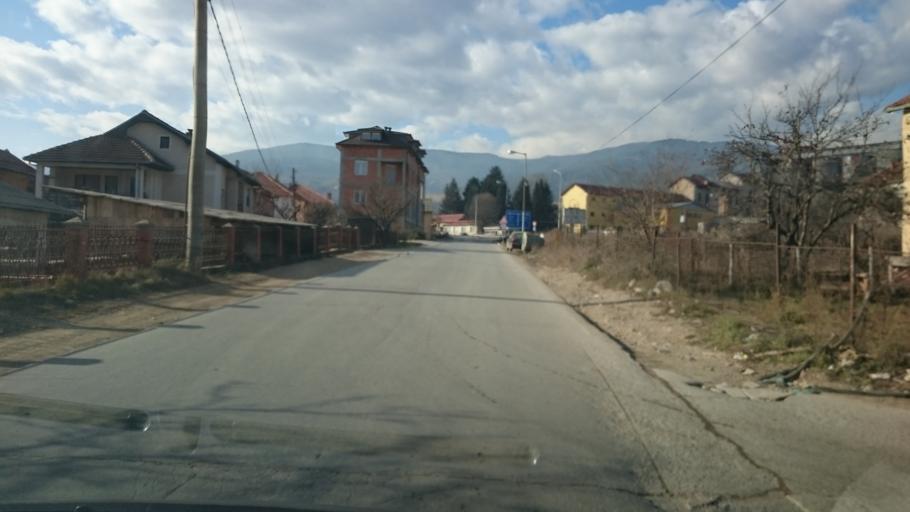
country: MK
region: Kicevo
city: Kicevo
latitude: 41.5007
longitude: 20.9541
